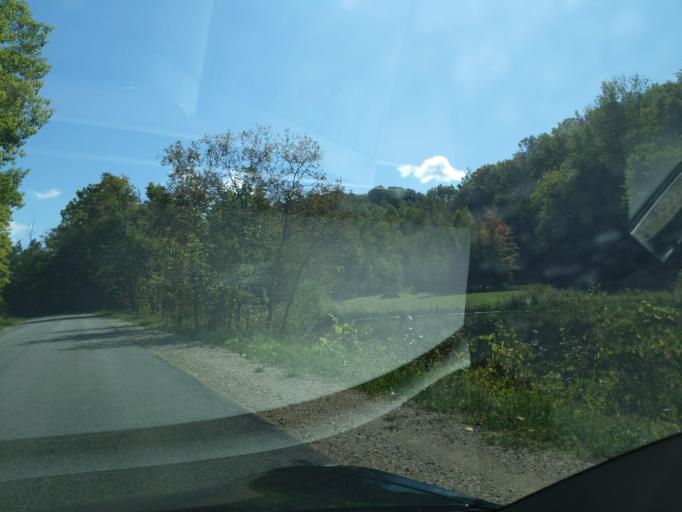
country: US
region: Michigan
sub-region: Antrim County
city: Elk Rapids
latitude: 44.9606
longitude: -85.3284
